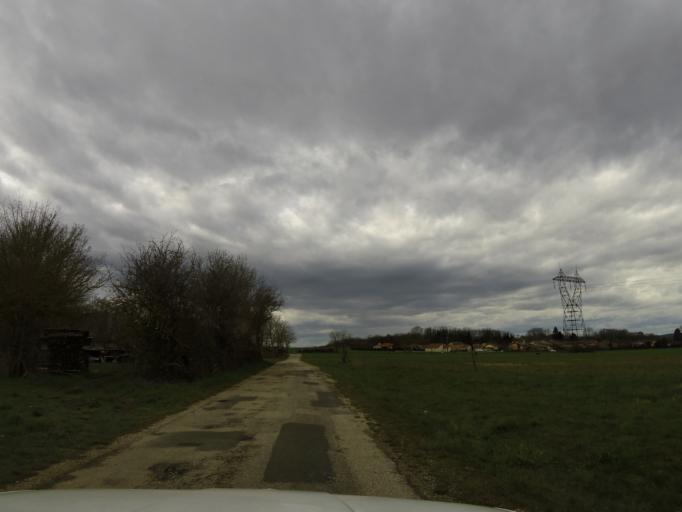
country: FR
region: Rhone-Alpes
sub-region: Departement de l'Ain
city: Leyment
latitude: 45.9170
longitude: 5.3021
